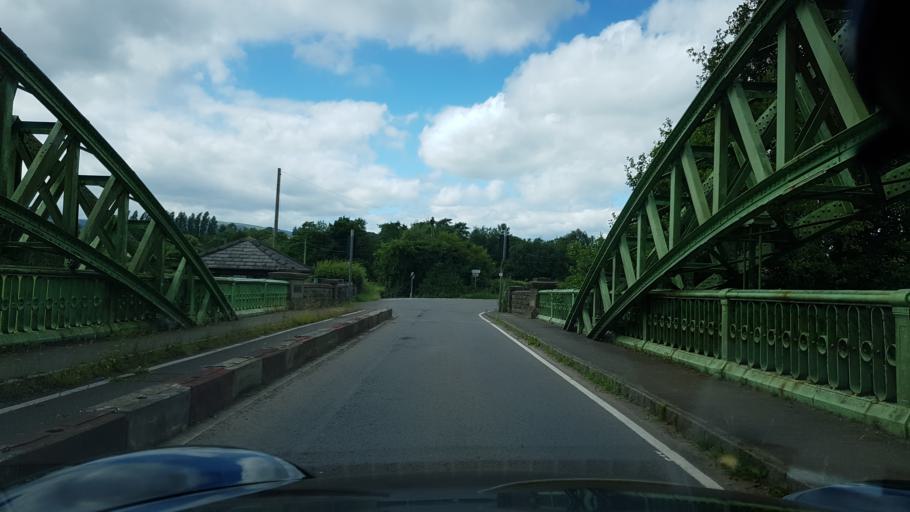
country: GB
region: Wales
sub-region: Monmouthshire
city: Usk
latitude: 51.7450
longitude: -2.9481
